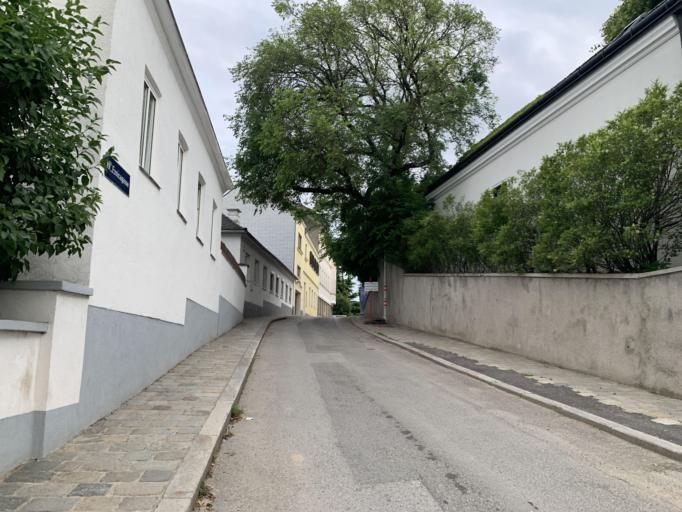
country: AT
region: Lower Austria
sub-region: Politischer Bezirk Korneuburg
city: Langenzersdorf
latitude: 48.2575
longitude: 16.3585
